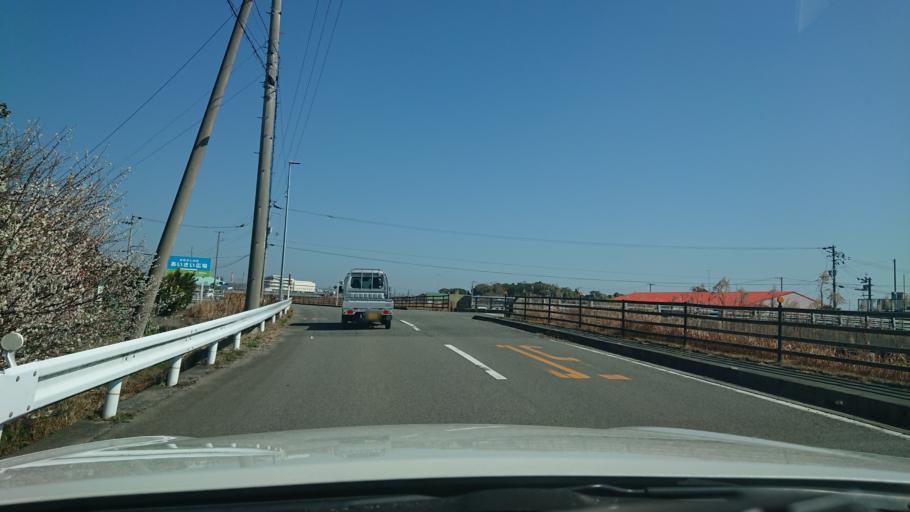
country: JP
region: Tokushima
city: Komatsushimacho
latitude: 33.9733
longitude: 134.6017
